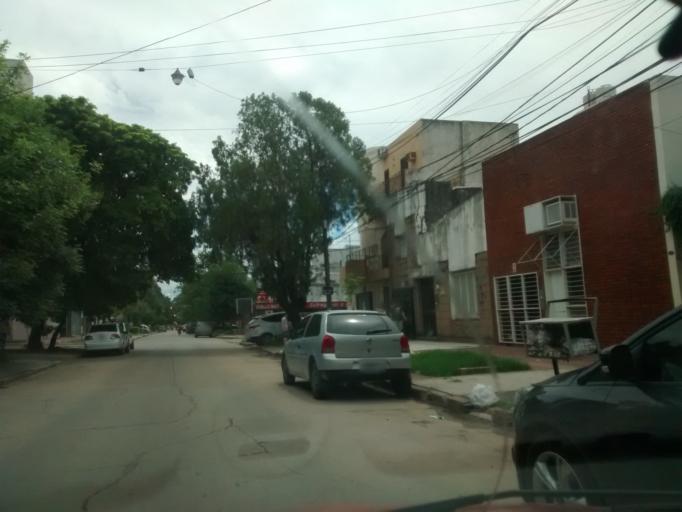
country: AR
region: Chaco
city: Resistencia
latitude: -27.4476
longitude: -58.9807
